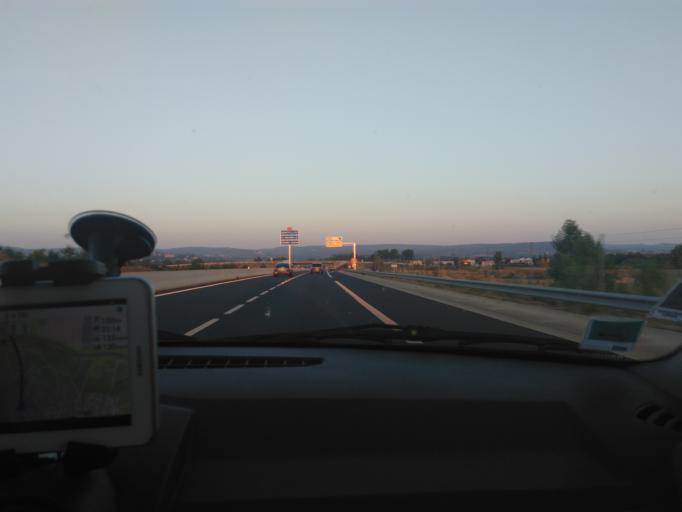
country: FR
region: Languedoc-Roussillon
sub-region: Departement de l'Herault
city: Saint-Andre-de-Sangonis
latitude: 43.6572
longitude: 3.5179
